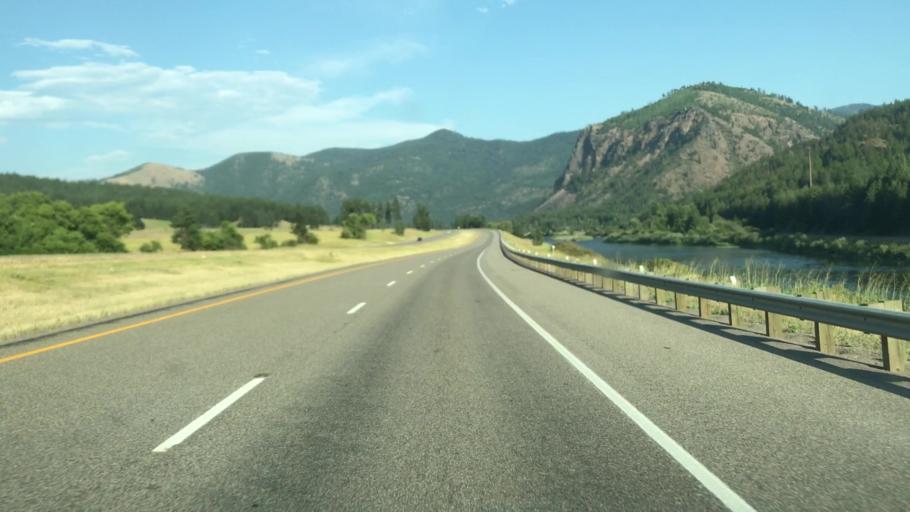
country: US
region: Montana
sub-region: Missoula County
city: Frenchtown
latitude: 46.9994
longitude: -114.4682
